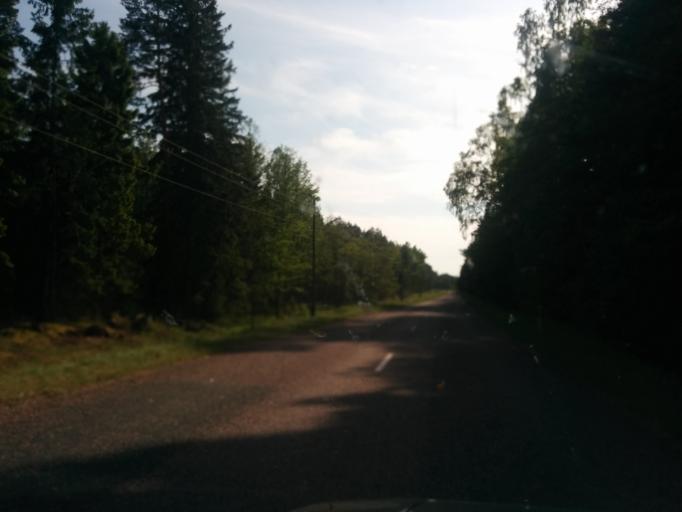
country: LV
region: Dundaga
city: Dundaga
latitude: 57.6638
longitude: 22.3001
